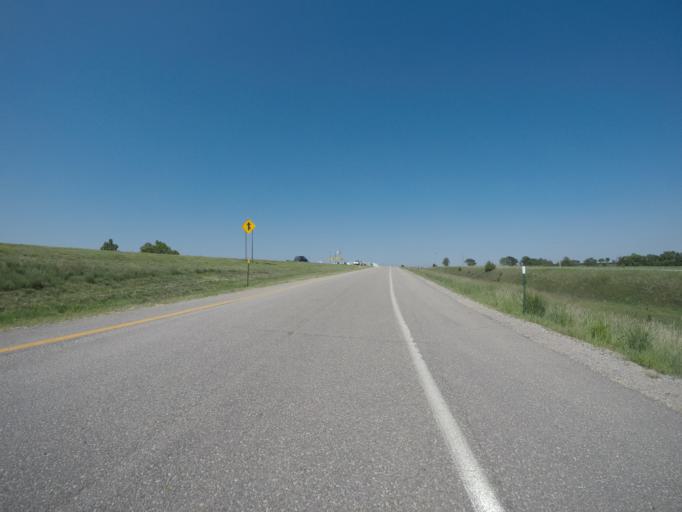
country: US
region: Kansas
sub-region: Dickinson County
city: Chapman
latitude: 38.9580
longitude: -97.1106
